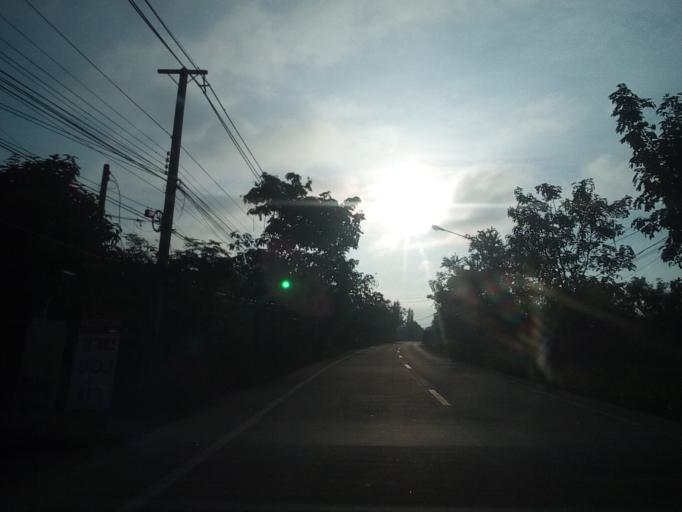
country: TH
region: Lamphun
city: Ban Thi
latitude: 18.6301
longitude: 99.0635
